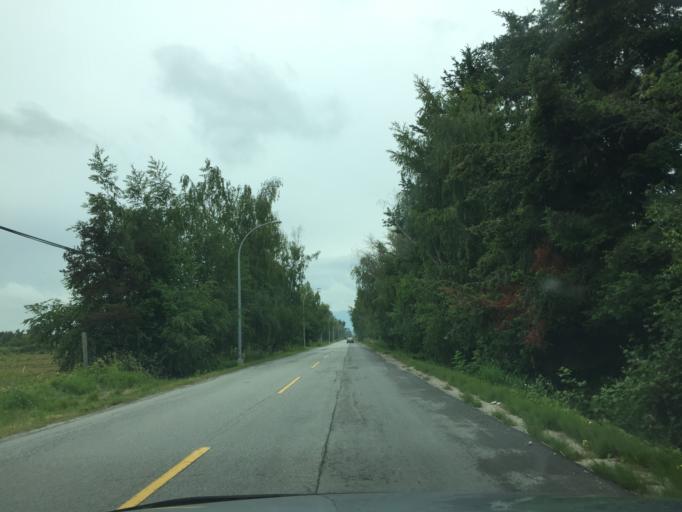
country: CA
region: British Columbia
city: Richmond
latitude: 49.1595
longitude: -123.0806
